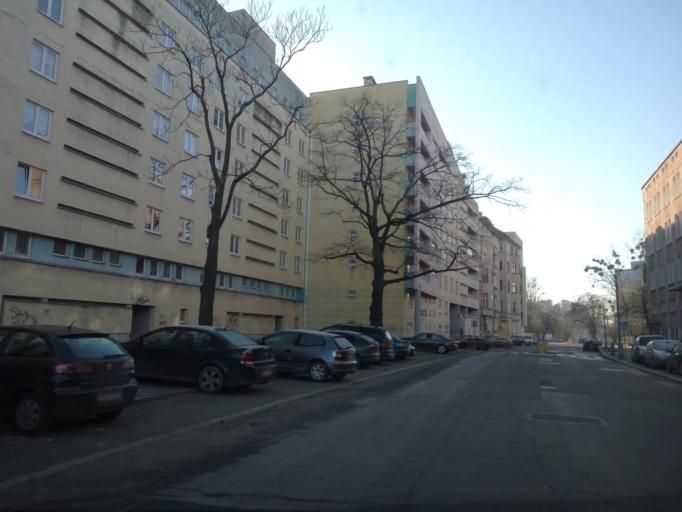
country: PL
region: Lower Silesian Voivodeship
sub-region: Powiat wroclawski
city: Wroclaw
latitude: 51.1006
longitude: 17.0183
